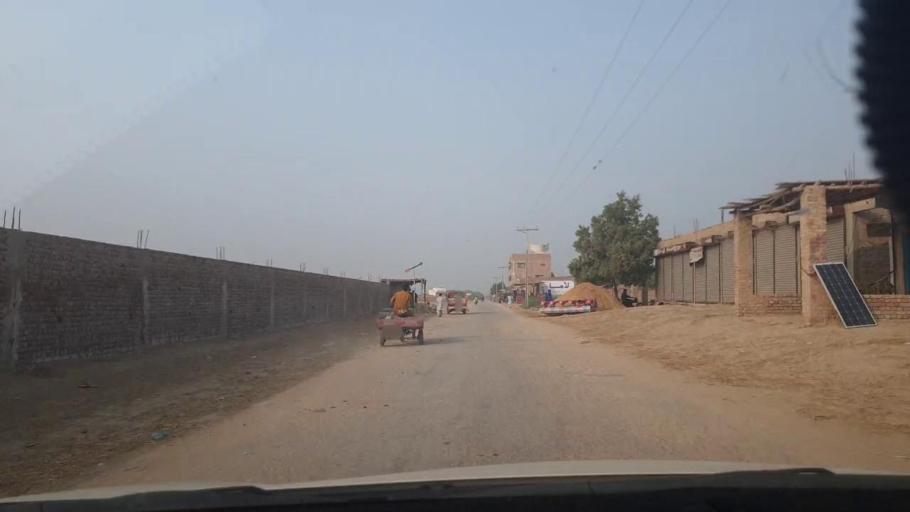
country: PK
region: Sindh
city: Bulri
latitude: 24.7581
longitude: 68.4193
